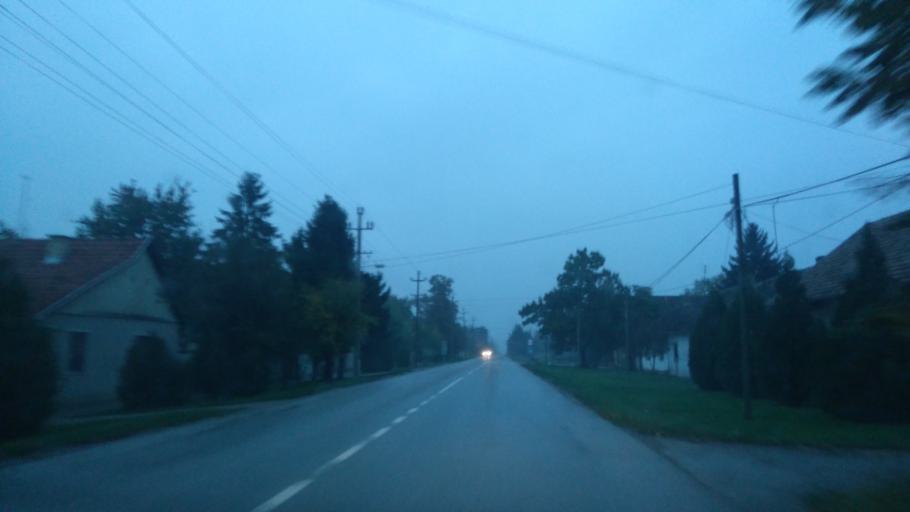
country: RS
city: Backo Petrovo Selo
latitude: 45.7140
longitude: 20.0899
